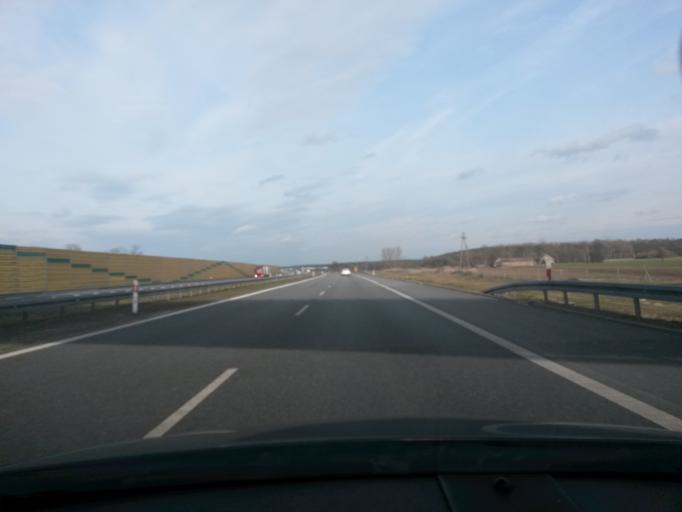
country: PL
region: Greater Poland Voivodeship
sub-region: Powiat koninski
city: Krzymow
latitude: 52.1431
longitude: 18.4057
